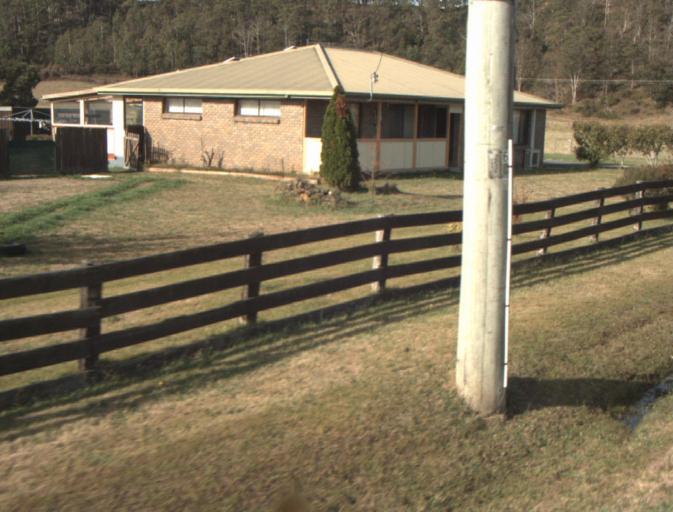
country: AU
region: Tasmania
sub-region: Launceston
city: Mayfield
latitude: -41.2478
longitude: 147.1466
